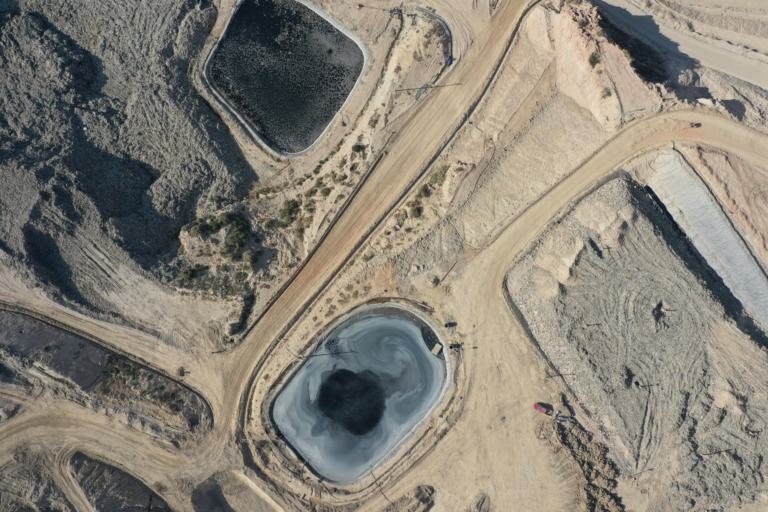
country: BO
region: La Paz
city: La Paz
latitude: -16.5586
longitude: -68.1280
